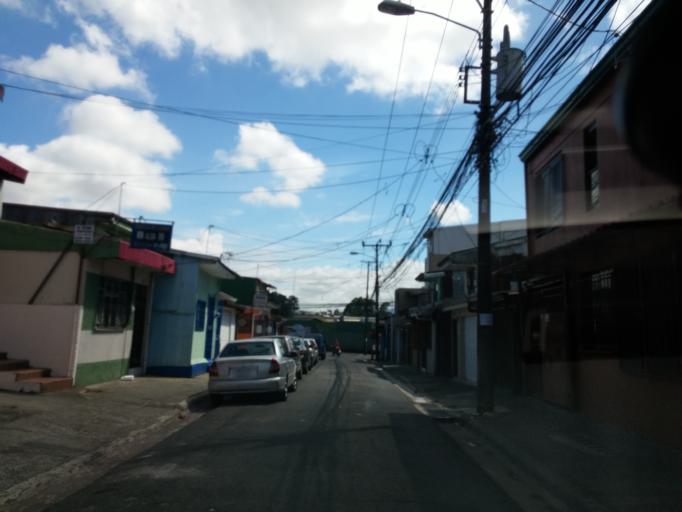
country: CR
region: San Jose
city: San Jose
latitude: 9.9279
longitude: -84.0963
